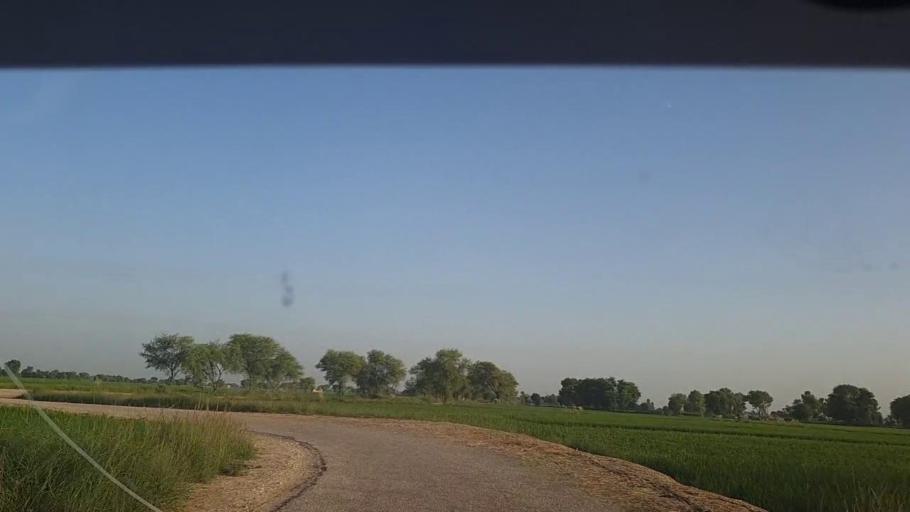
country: PK
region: Sindh
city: Thul
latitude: 28.1262
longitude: 68.8933
